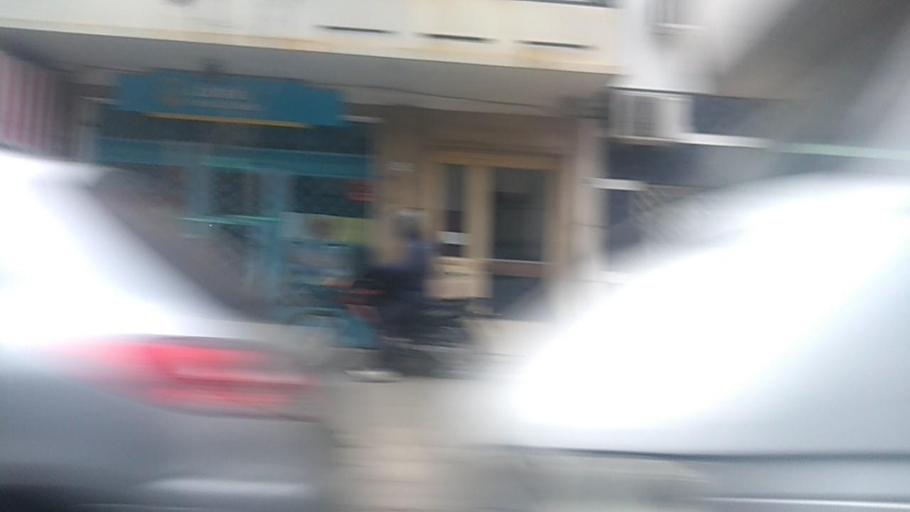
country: AR
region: Buenos Aires F.D.
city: Villa Santa Rita
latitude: -34.6041
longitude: -58.5017
